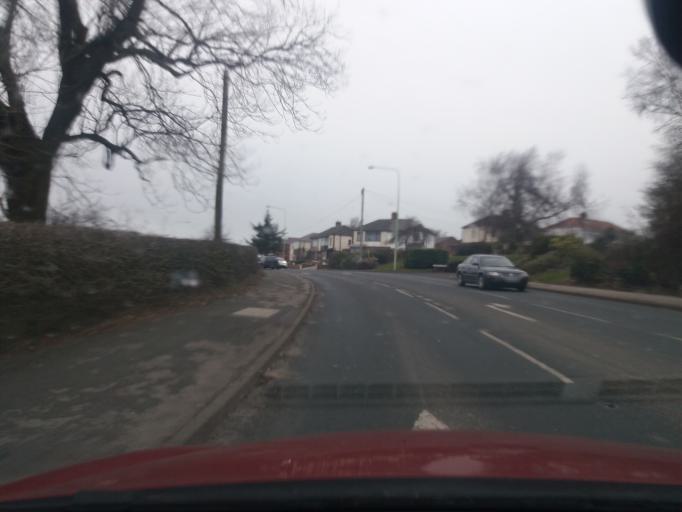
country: GB
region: England
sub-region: Lancashire
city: Chorley
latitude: 53.6680
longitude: -2.6152
